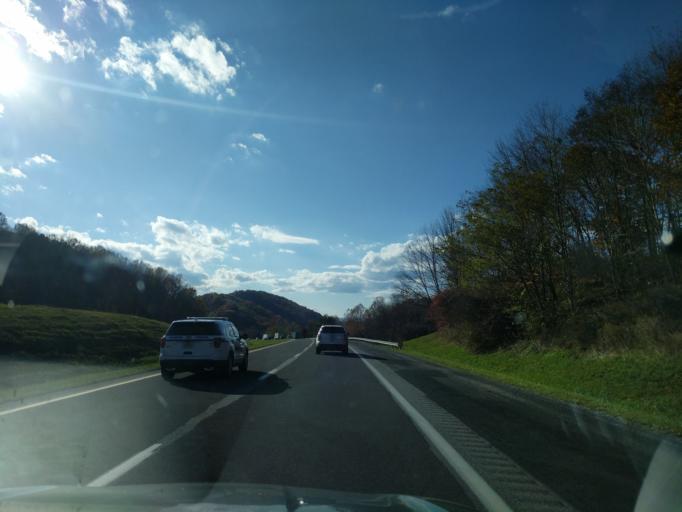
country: US
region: Virginia
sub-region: Wythe County
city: Wytheville
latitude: 36.9497
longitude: -81.1353
